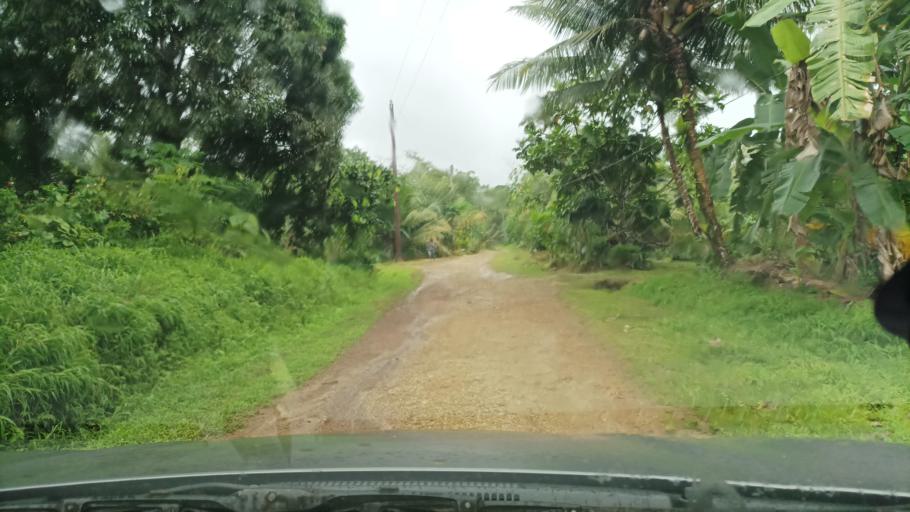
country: FM
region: Pohnpei
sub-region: Sokehs Municipality
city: Palikir - National Government Center
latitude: 6.8532
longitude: 158.1836
